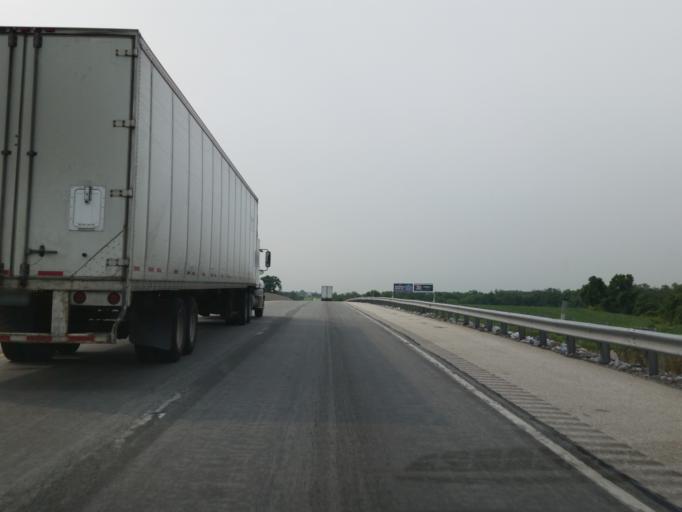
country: US
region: Pennsylvania
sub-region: York County
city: Emigsville
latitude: 40.0473
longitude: -76.7508
